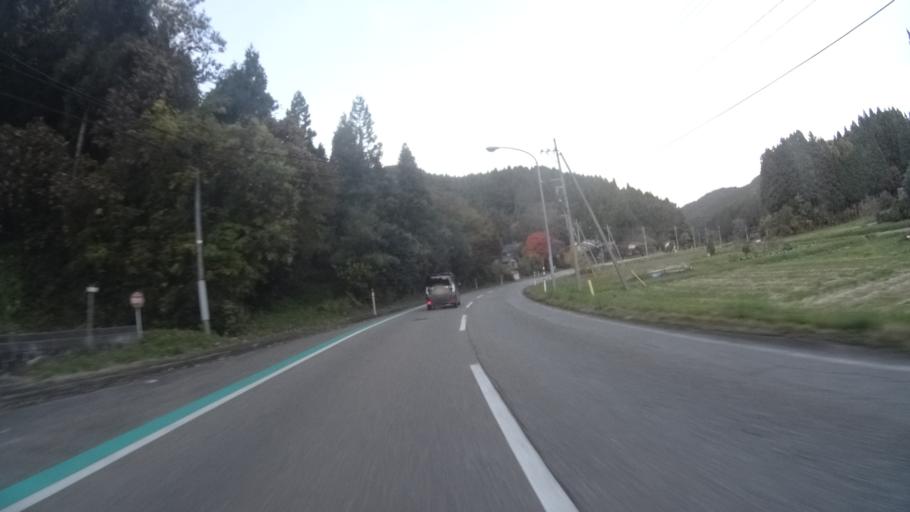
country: JP
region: Ishikawa
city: Nanao
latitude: 37.3122
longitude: 136.7988
